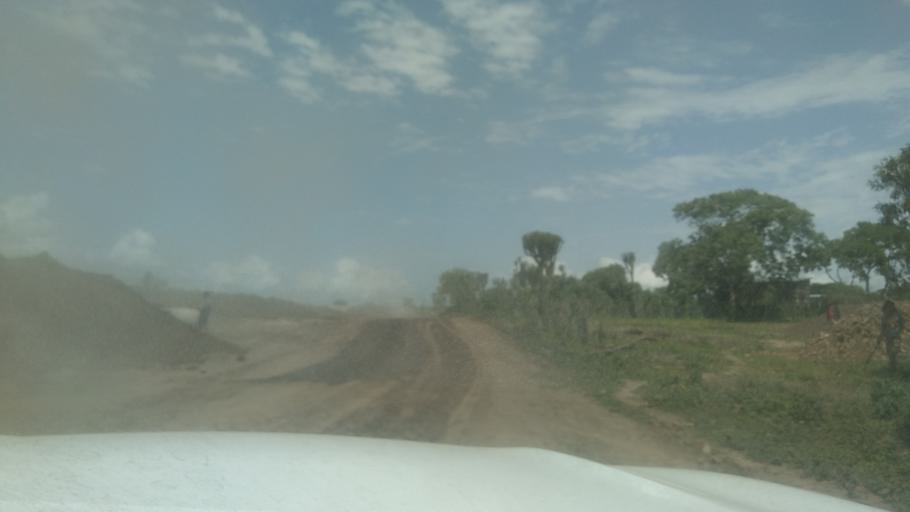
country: ET
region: Oromiya
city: Shashemene
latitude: 7.2792
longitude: 38.6044
